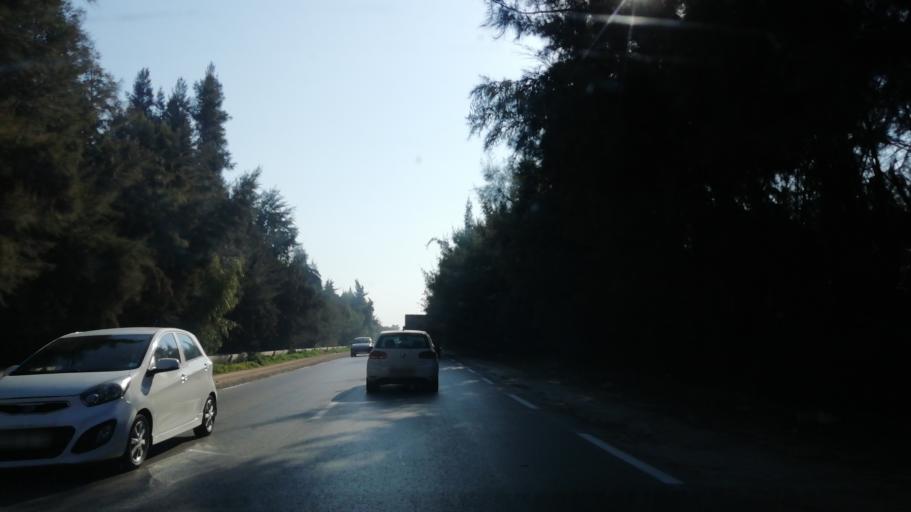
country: DZ
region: Relizane
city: Relizane
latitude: 35.7313
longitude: 0.4721
